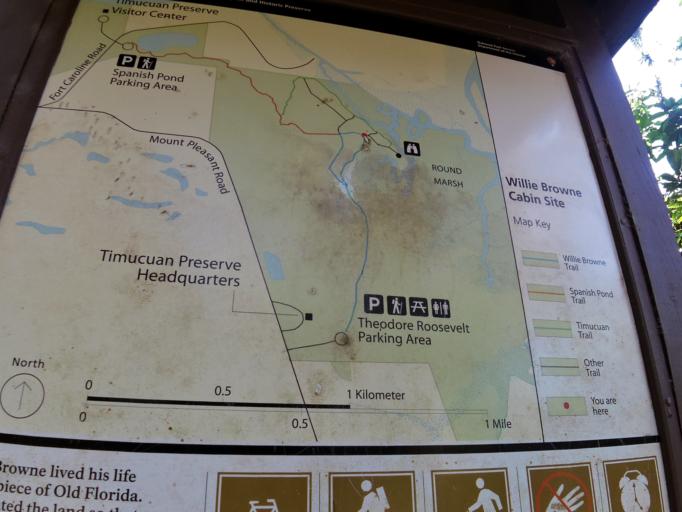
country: US
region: Florida
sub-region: Duval County
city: Atlantic Beach
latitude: 30.3799
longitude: -81.4824
